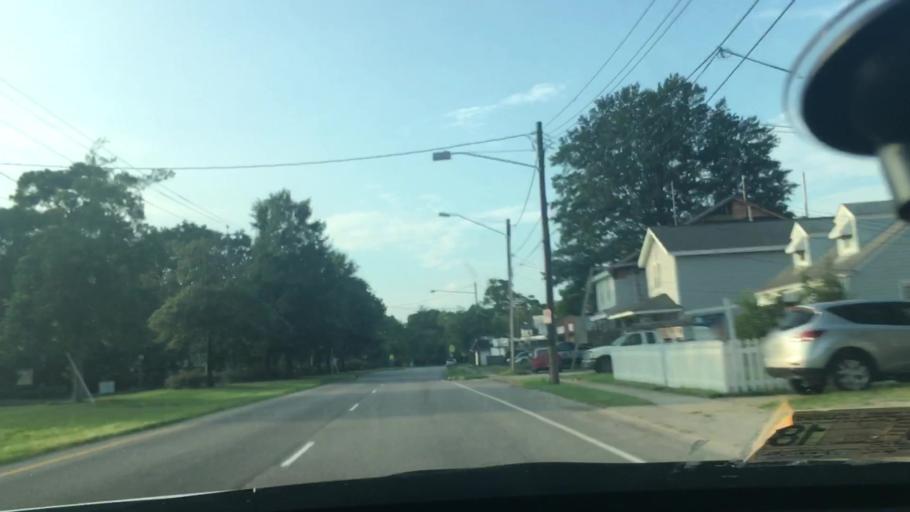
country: US
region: Virginia
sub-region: City of Norfolk
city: Norfolk
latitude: 36.9413
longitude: -76.2454
